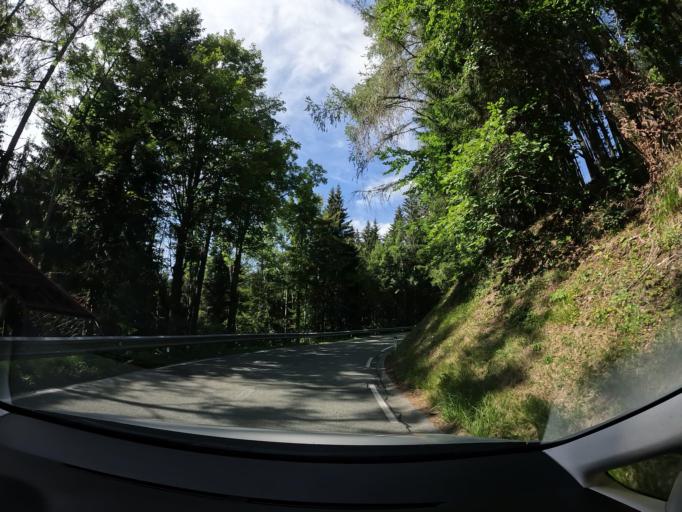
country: AT
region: Carinthia
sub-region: Politischer Bezirk Feldkirchen
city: Glanegg
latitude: 46.7337
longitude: 14.2158
